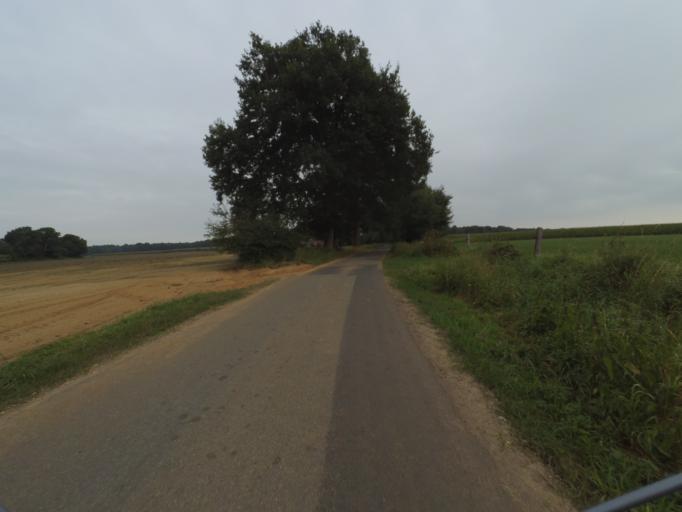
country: DE
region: Lower Saxony
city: Isterberg
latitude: 52.3338
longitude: 7.0626
